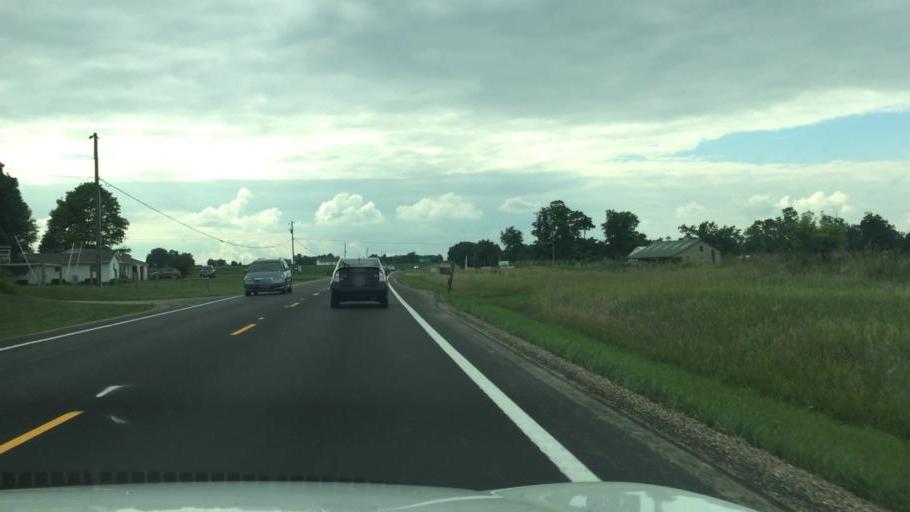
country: US
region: Ohio
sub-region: Champaign County
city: Urbana
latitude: 40.0869
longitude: -83.6833
